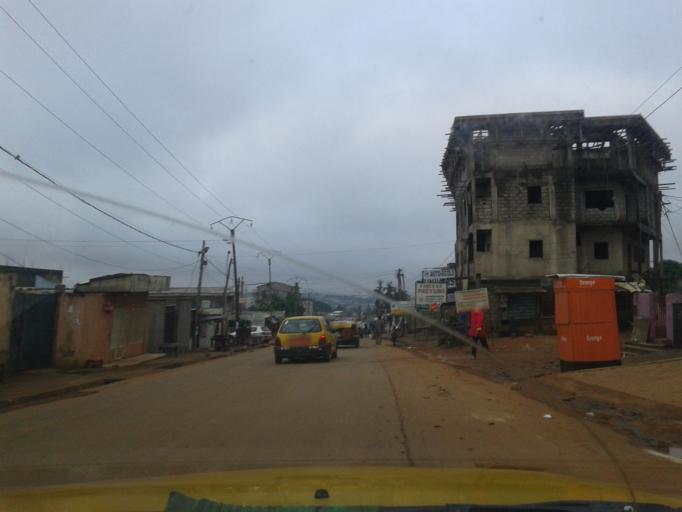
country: CM
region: Centre
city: Yaounde
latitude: 3.8990
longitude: 11.5322
